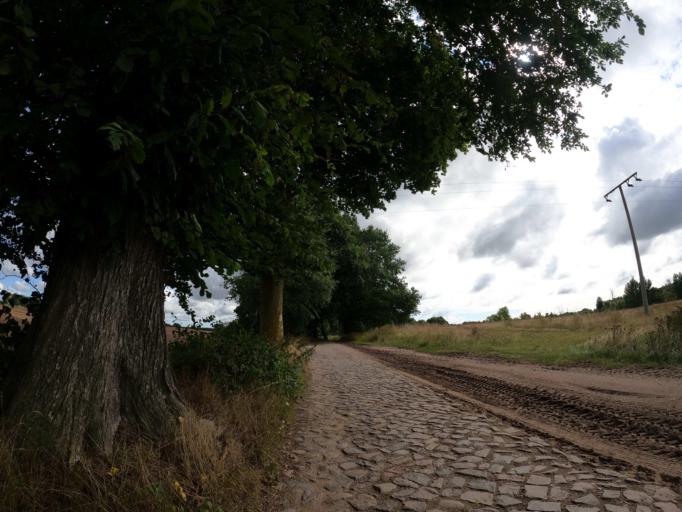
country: DE
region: Mecklenburg-Vorpommern
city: Samtens
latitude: 54.3605
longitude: 13.3149
